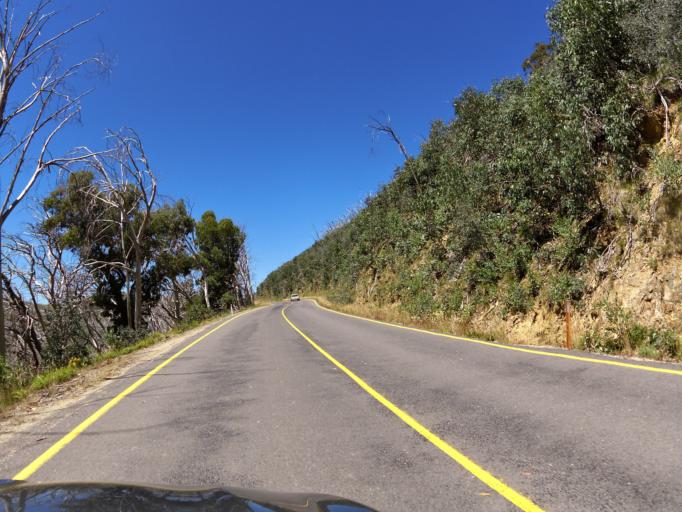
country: AU
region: Victoria
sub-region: Alpine
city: Mount Beauty
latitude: -37.0028
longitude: 147.0736
